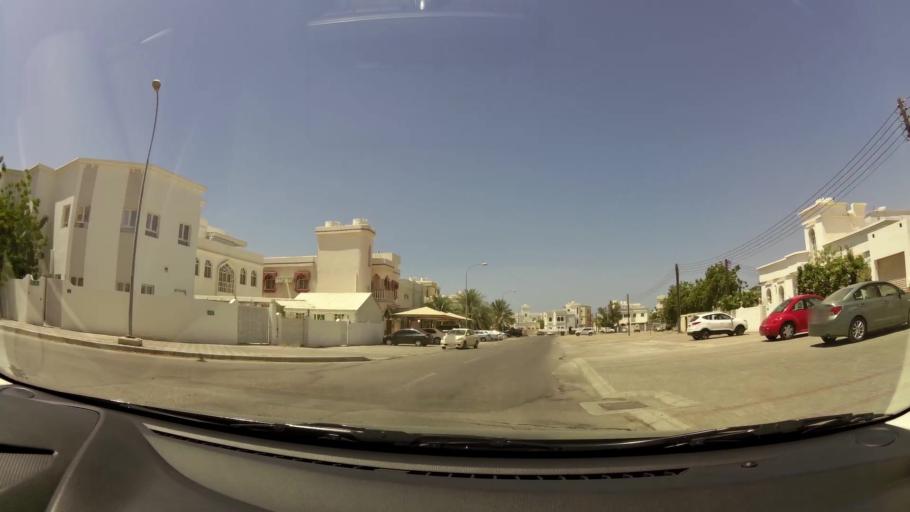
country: OM
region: Muhafazat Masqat
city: Bawshar
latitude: 23.5922
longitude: 58.3793
